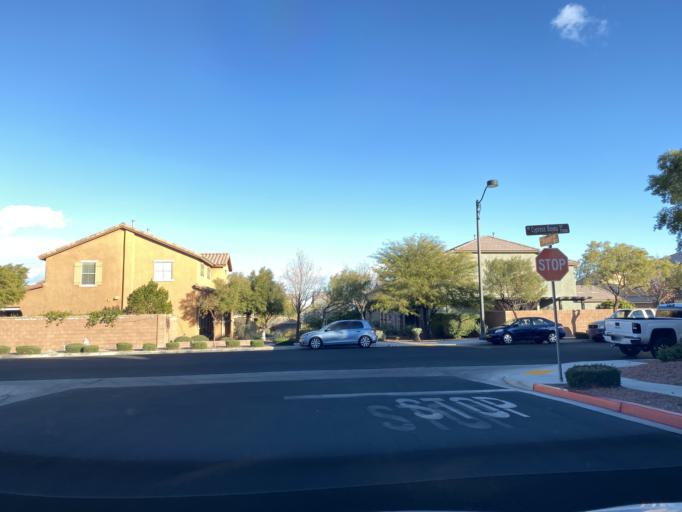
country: US
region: Nevada
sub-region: Clark County
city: Summerlin South
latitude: 36.2975
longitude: -115.3310
